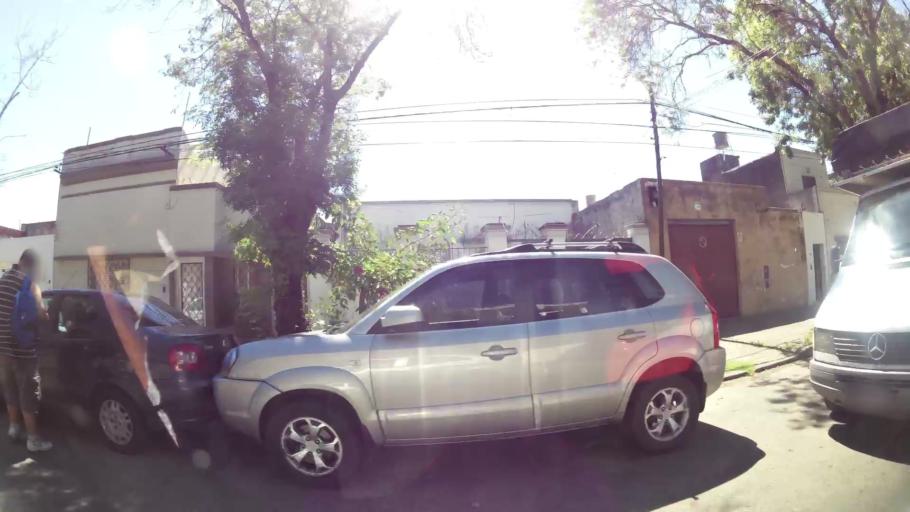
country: AR
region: Santa Fe
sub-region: Departamento de Rosario
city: Rosario
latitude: -32.9445
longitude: -60.6834
